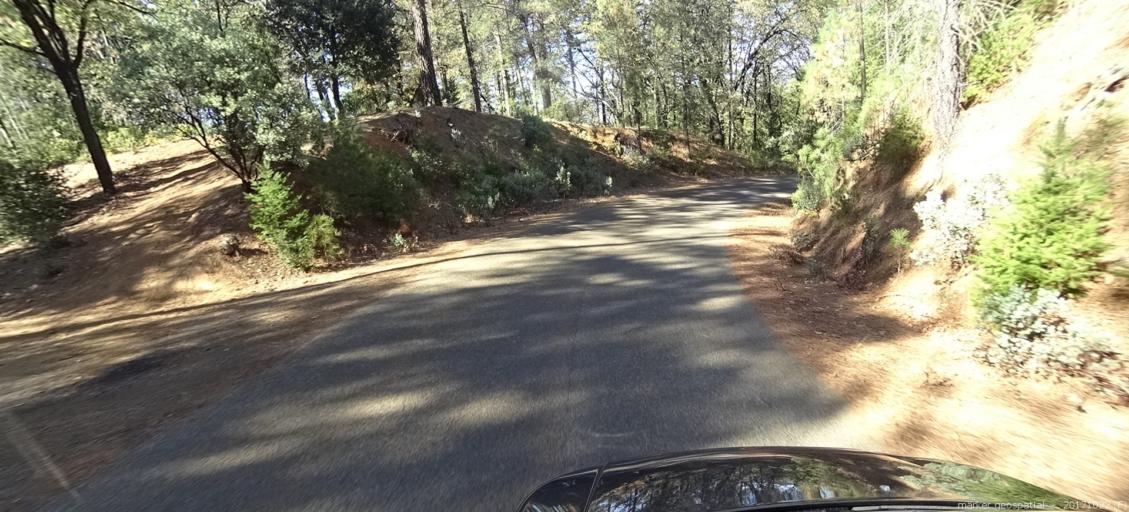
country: US
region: California
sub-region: Shasta County
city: Shasta Lake
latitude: 40.8847
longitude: -122.3693
